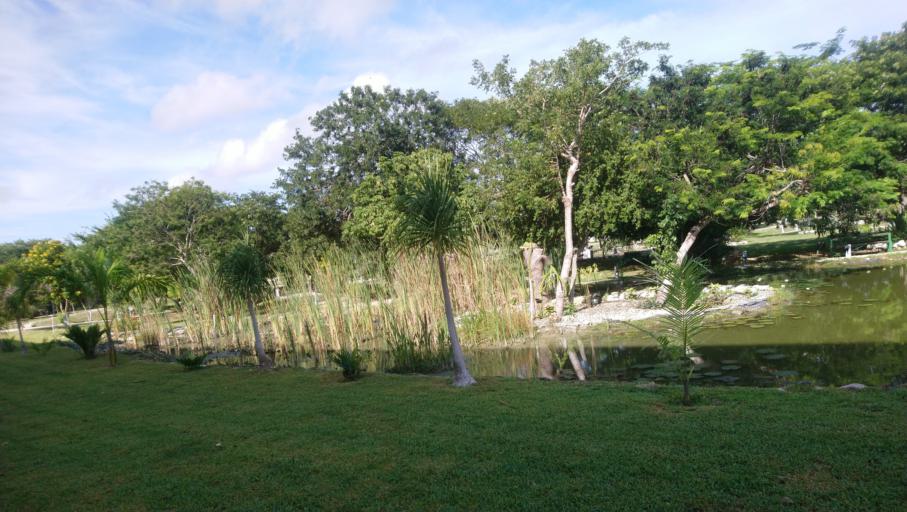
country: MX
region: Yucatan
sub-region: Merida
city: Sierra Papacal
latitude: 21.1311
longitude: -89.7809
